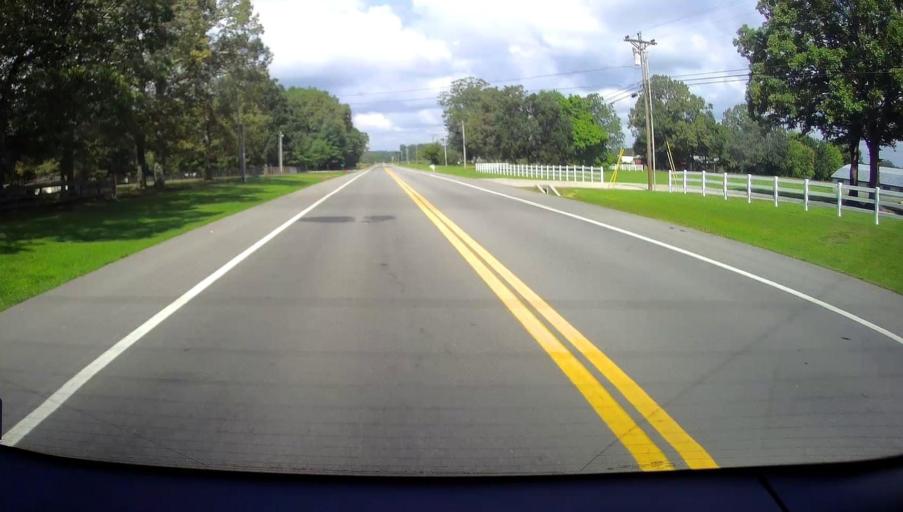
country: US
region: Tennessee
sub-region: Coffee County
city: New Union
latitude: 35.5196
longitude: -86.1438
